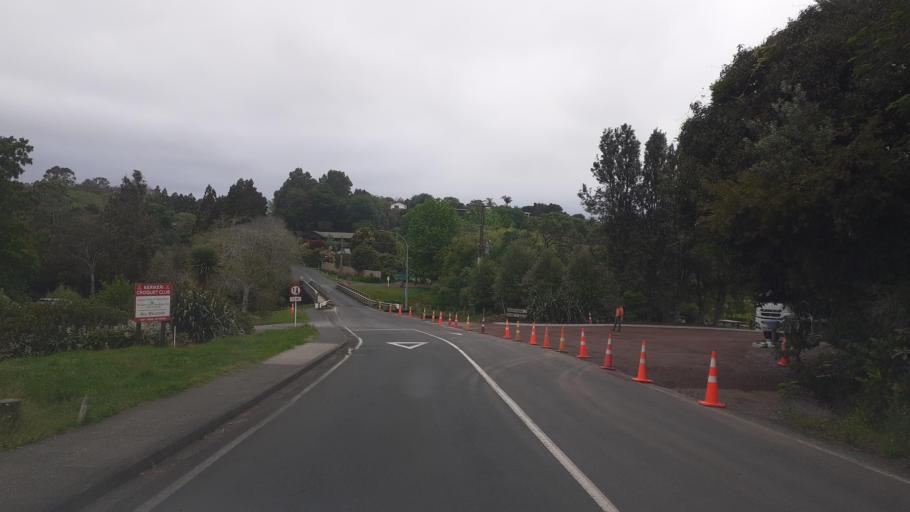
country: NZ
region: Northland
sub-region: Far North District
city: Kerikeri
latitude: -35.2035
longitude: 173.9674
